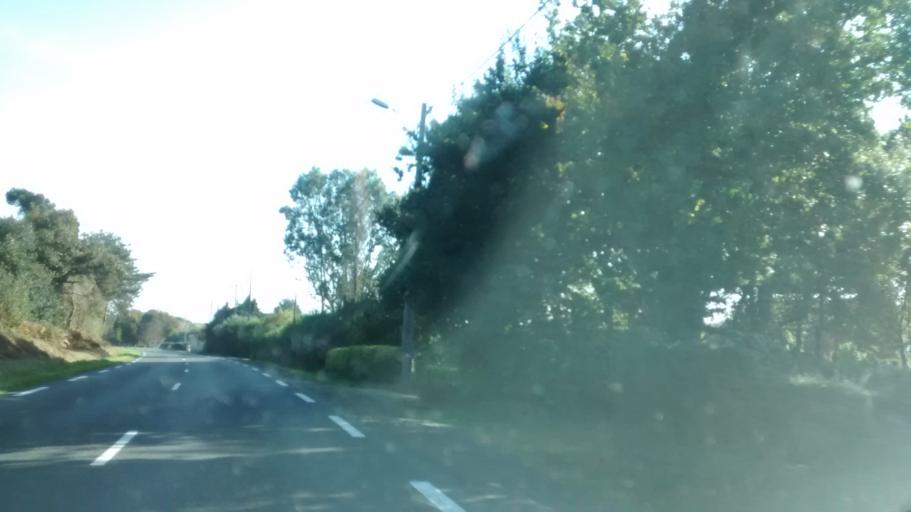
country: FR
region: Brittany
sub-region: Departement des Cotes-d'Armor
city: Pleumeur-Bodou
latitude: 48.7600
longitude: -3.5389
